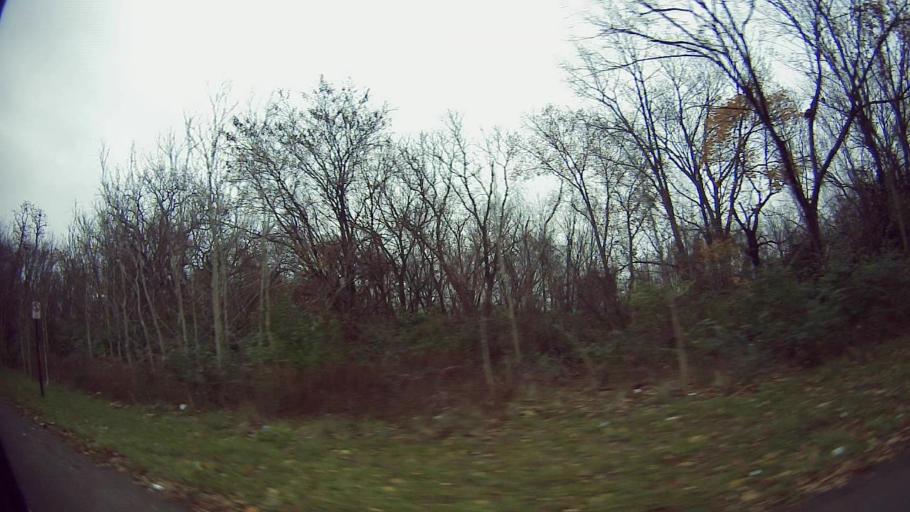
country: US
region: Michigan
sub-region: Wayne County
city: Redford
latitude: 42.3739
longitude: -83.2609
